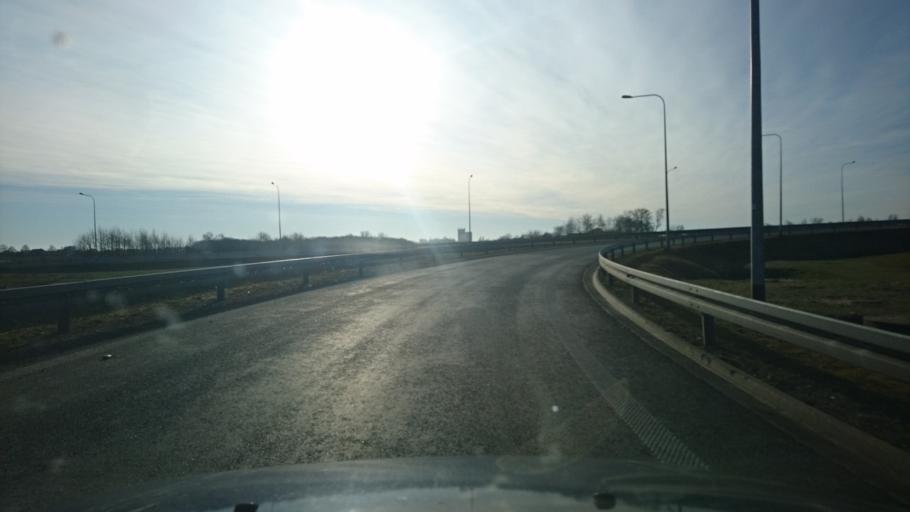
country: PL
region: Greater Poland Voivodeship
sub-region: Powiat kepinski
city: Kepno
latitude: 51.3147
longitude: 18.0097
